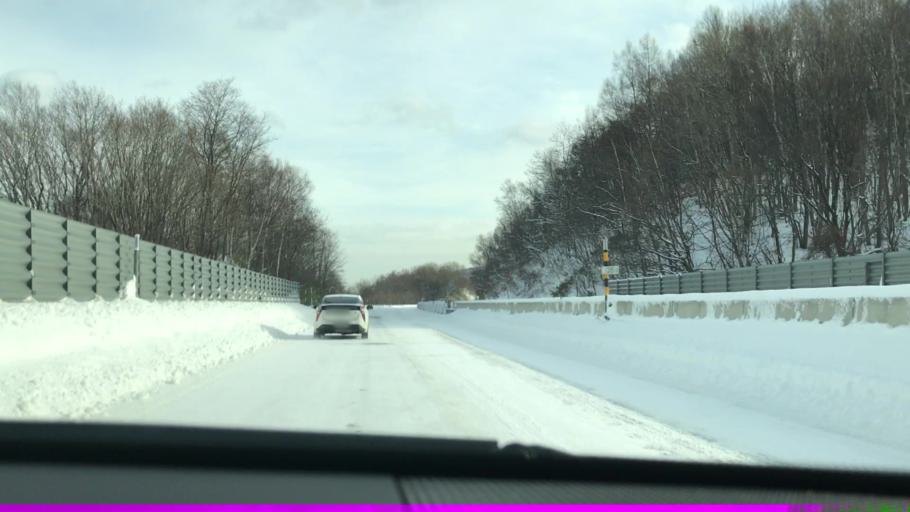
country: JP
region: Hokkaido
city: Otaru
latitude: 43.1456
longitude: 141.1372
